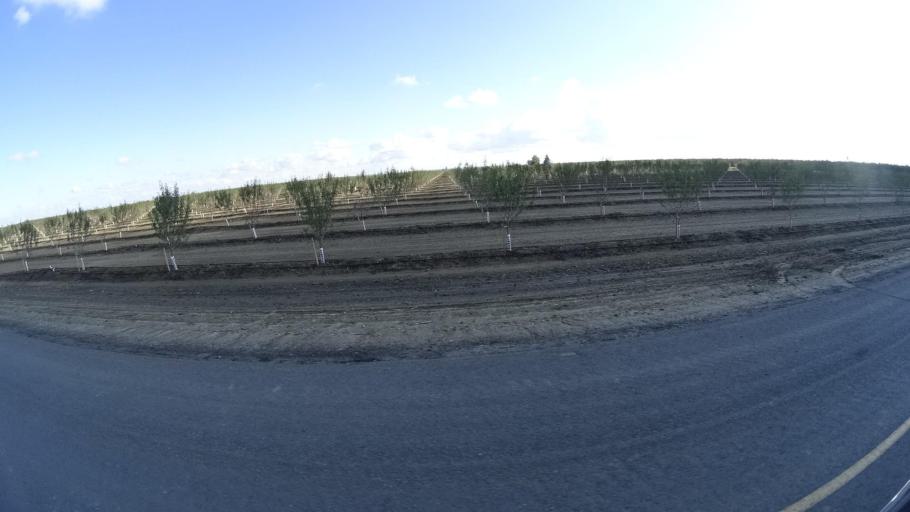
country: US
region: California
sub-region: Kern County
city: McFarland
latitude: 35.6616
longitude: -119.2588
